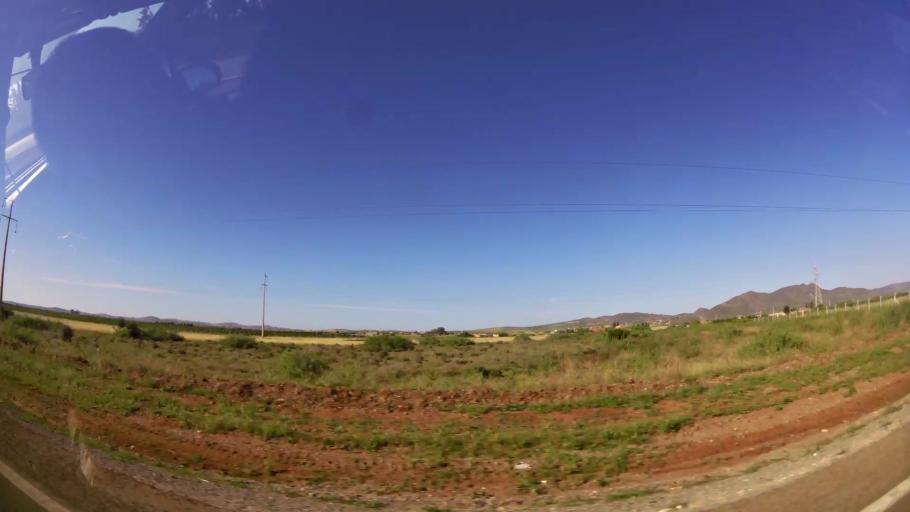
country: MA
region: Oriental
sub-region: Berkane-Taourirt
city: Ahfir
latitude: 34.9916
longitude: -2.1582
